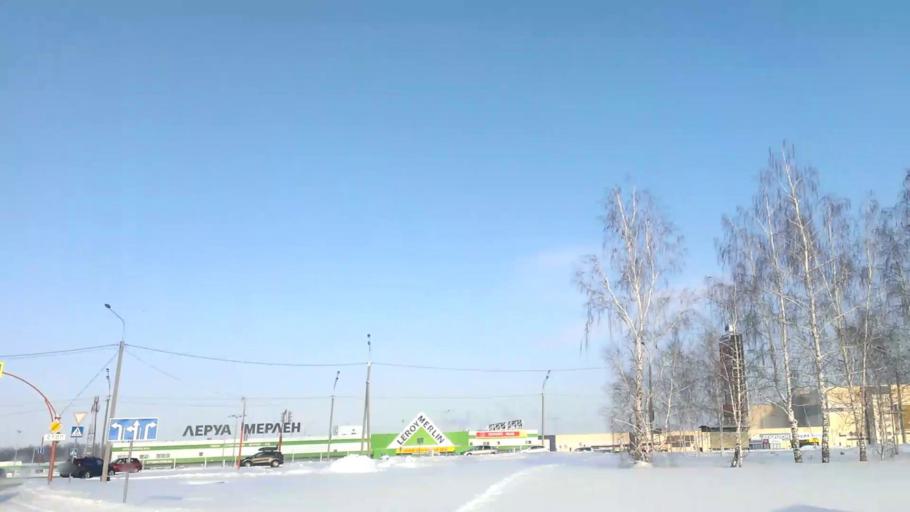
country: RU
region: Altai Krai
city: Novosilikatnyy
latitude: 53.3475
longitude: 83.6313
